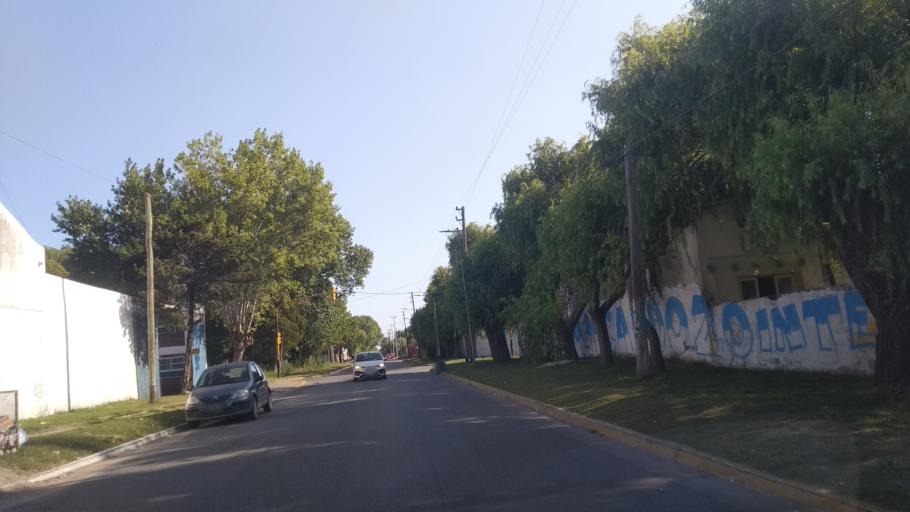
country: AR
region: Buenos Aires
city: Mar del Tuyu
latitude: -36.5339
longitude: -56.7132
